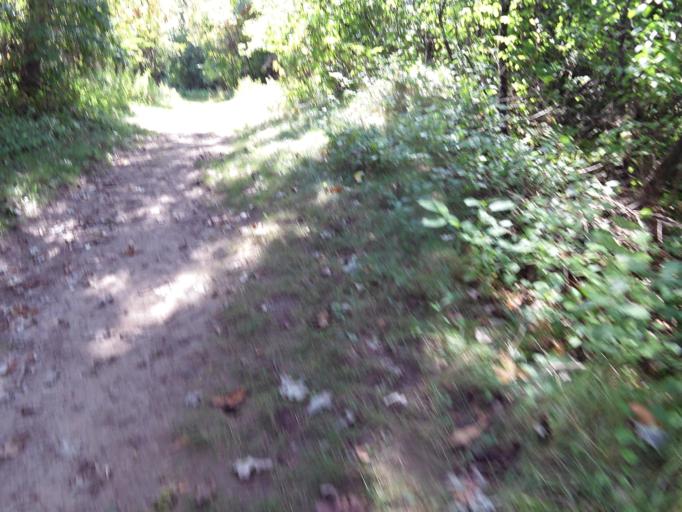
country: US
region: Minnesota
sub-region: Washington County
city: Afton
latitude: 44.8634
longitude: -92.8011
